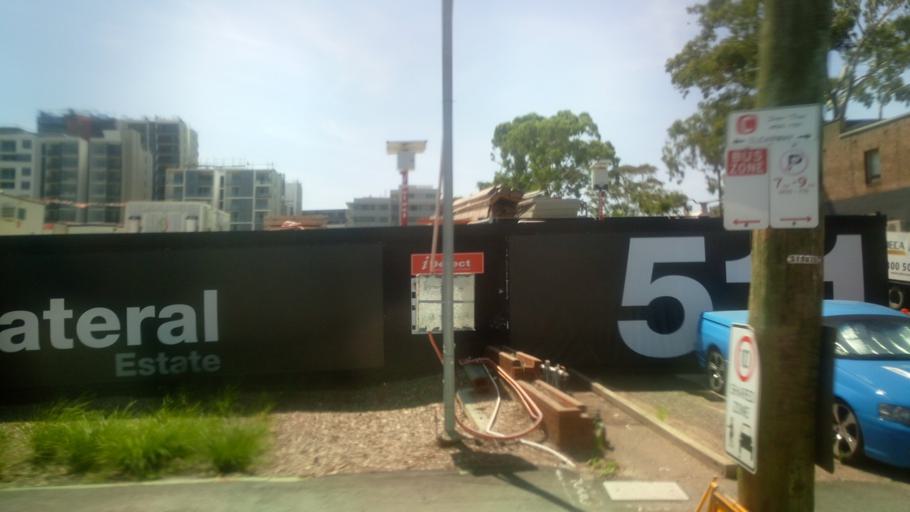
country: AU
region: New South Wales
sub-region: City of Sydney
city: Alexandria
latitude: -33.9088
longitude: 151.2029
